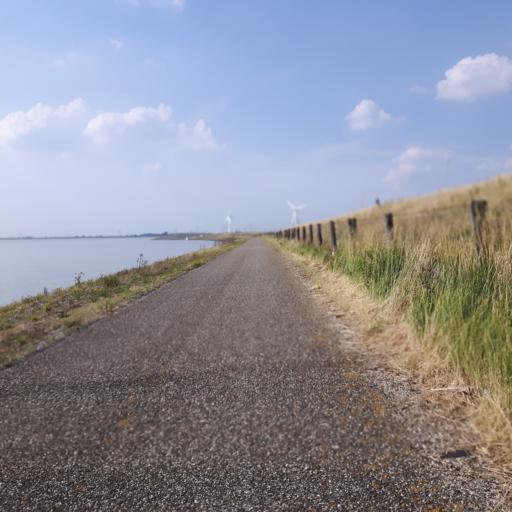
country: NL
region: Zeeland
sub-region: Gemeente Reimerswaal
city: Yerseke
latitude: 51.4503
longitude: 3.9952
